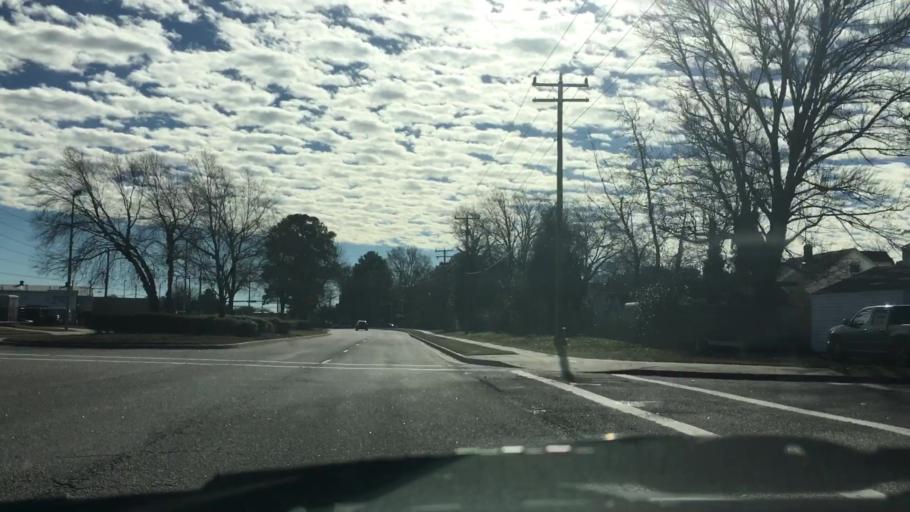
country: US
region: Virginia
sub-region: City of Norfolk
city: Norfolk
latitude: 36.8699
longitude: -76.2507
